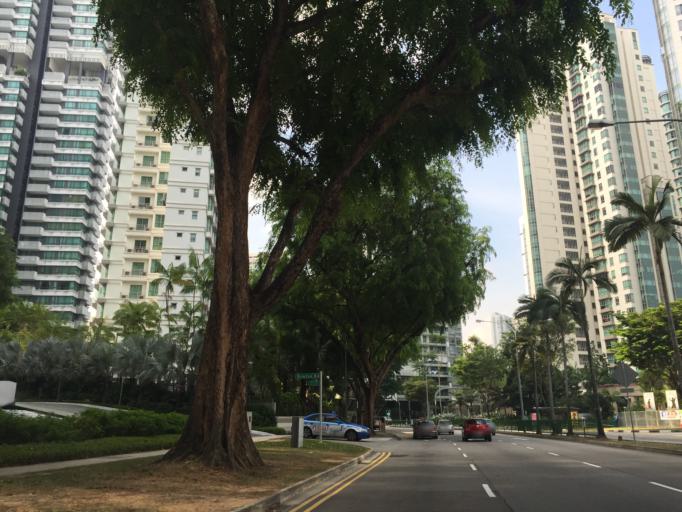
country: SG
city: Singapore
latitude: 1.3140
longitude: 103.8400
